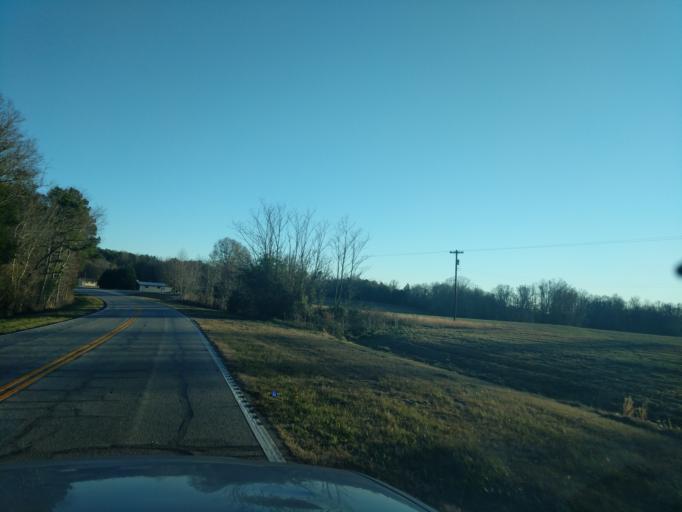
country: US
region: Georgia
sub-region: Hart County
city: Reed Creek
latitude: 34.5547
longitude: -82.8686
